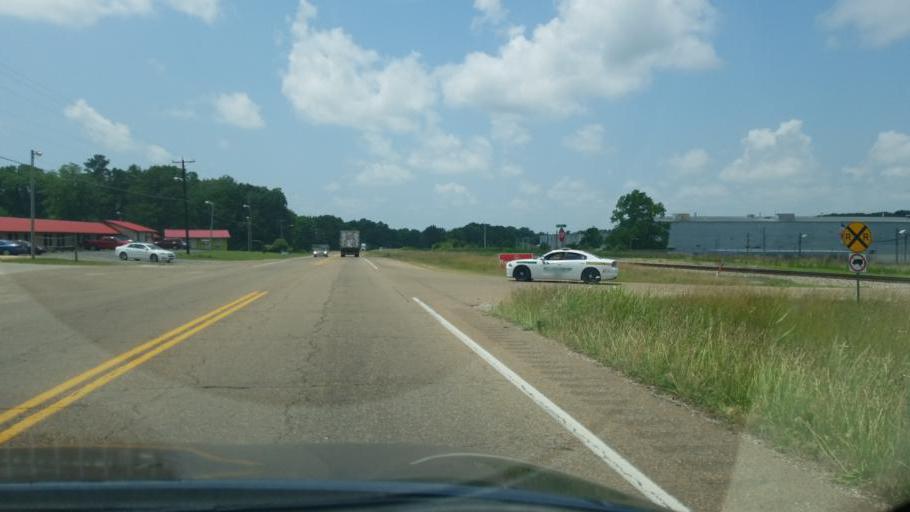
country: US
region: Tennessee
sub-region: Carroll County
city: Huntingdon
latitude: 36.0176
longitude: -88.3780
